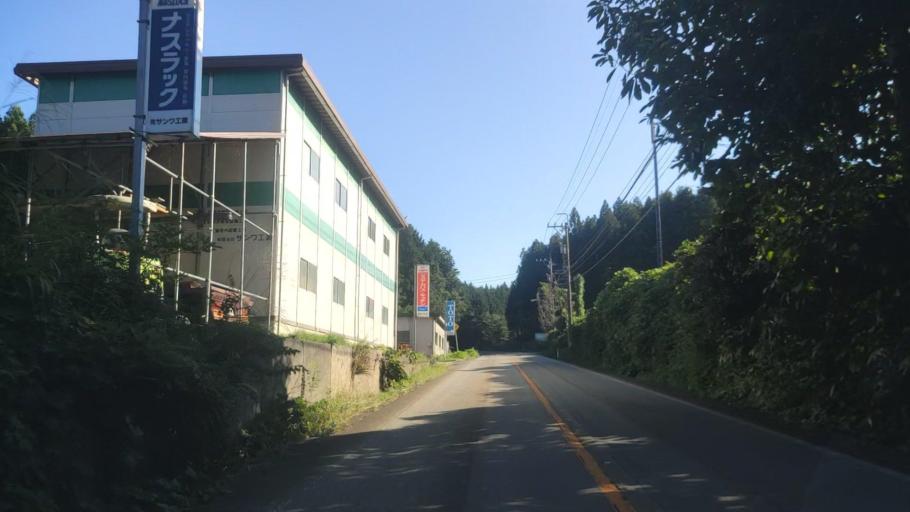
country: JP
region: Ishikawa
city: Nanao
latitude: 37.1352
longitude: 136.8629
